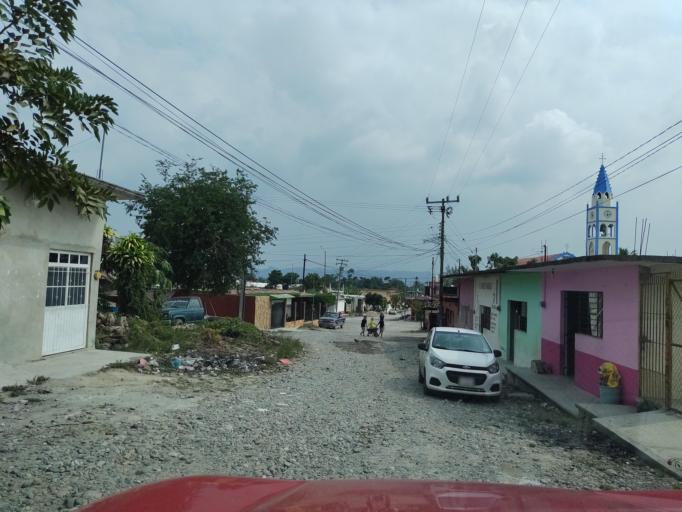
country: MX
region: Veracruz
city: Agua Dulce
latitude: 20.3632
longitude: -97.2957
